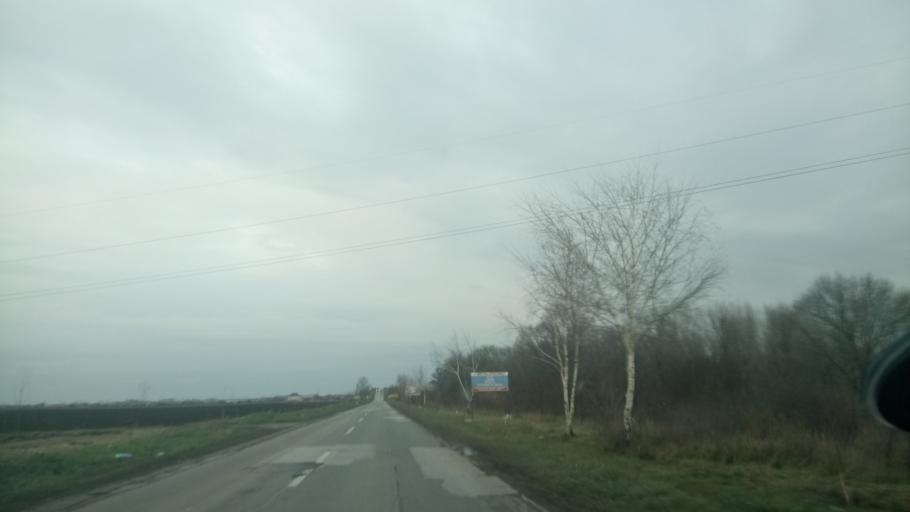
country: RS
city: Vojka
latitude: 44.9601
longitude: 20.1593
